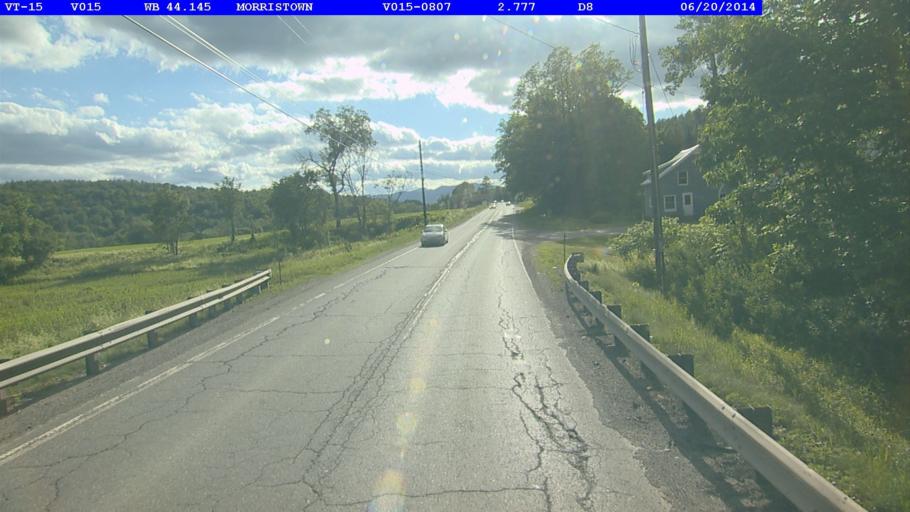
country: US
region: Vermont
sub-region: Lamoille County
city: Morrisville
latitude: 44.5659
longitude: -72.5590
